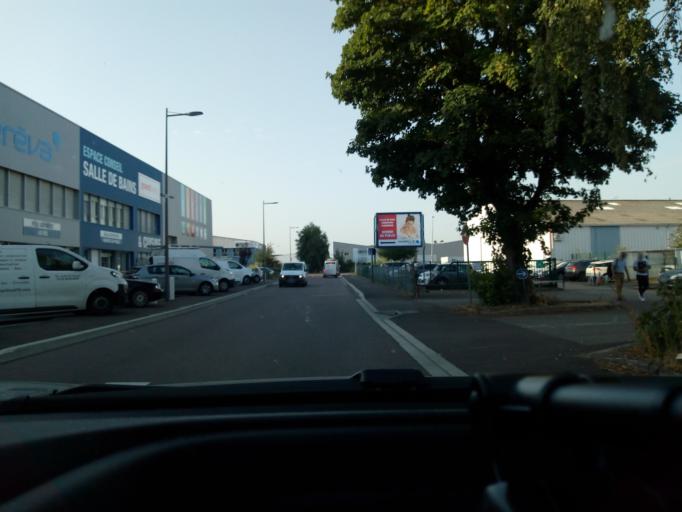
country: FR
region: Haute-Normandie
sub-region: Departement de la Seine-Maritime
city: Saint-Etienne-du-Rouvray
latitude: 49.3996
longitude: 1.1147
